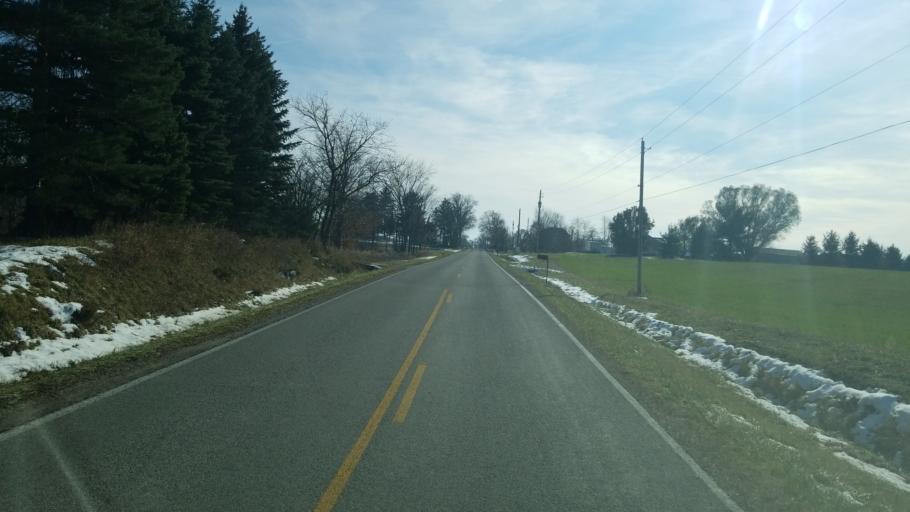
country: US
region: Ohio
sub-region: Huron County
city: Wakeman
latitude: 41.2235
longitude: -82.3609
